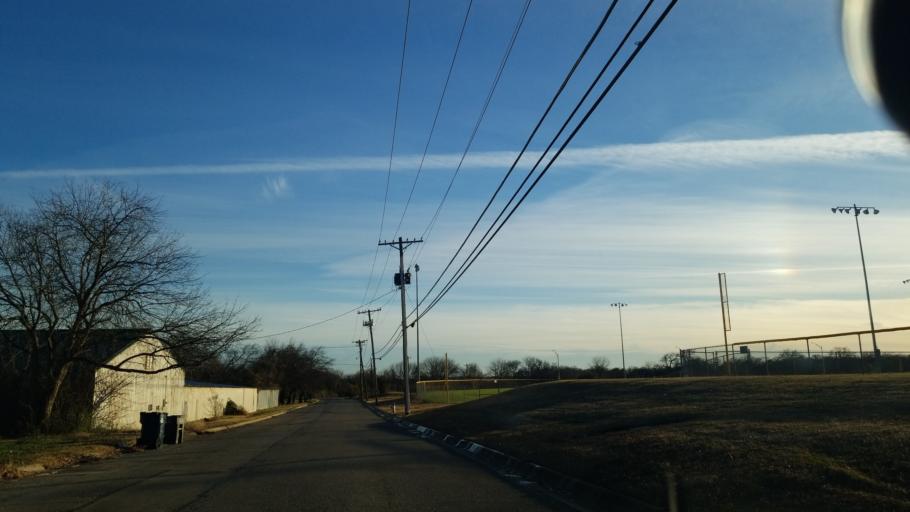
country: US
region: Texas
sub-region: Denton County
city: Denton
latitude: 33.1896
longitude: -97.1418
